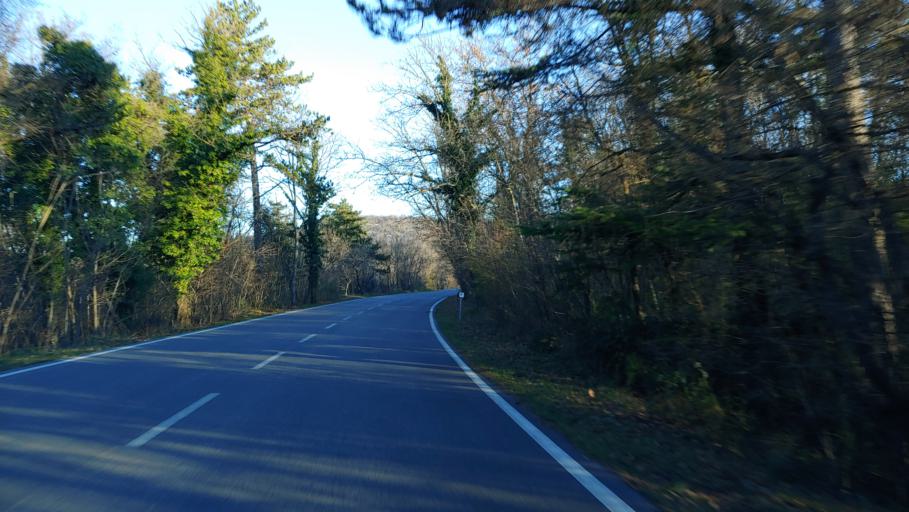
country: IT
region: Friuli Venezia Giulia
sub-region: Provincia di Trieste
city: Zolla
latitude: 45.7047
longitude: 13.8010
